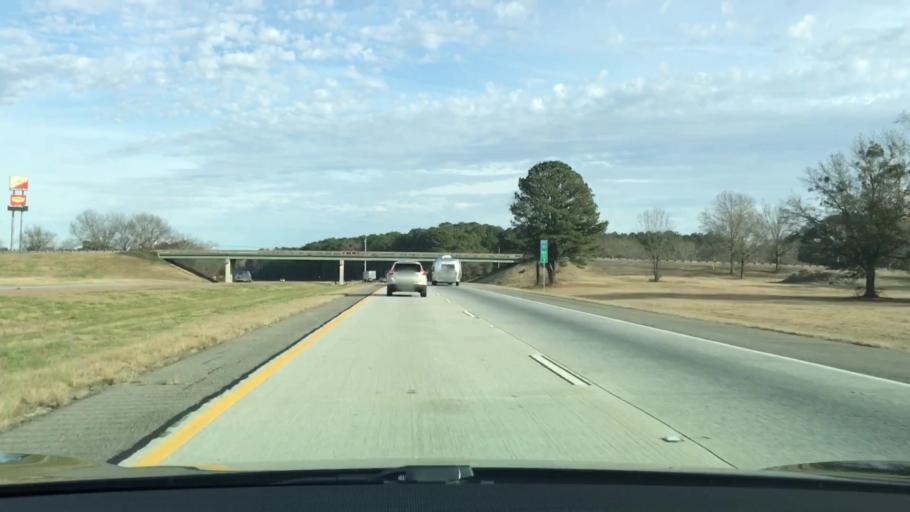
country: US
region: Georgia
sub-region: Greene County
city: Union Point
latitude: 33.5458
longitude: -83.0823
